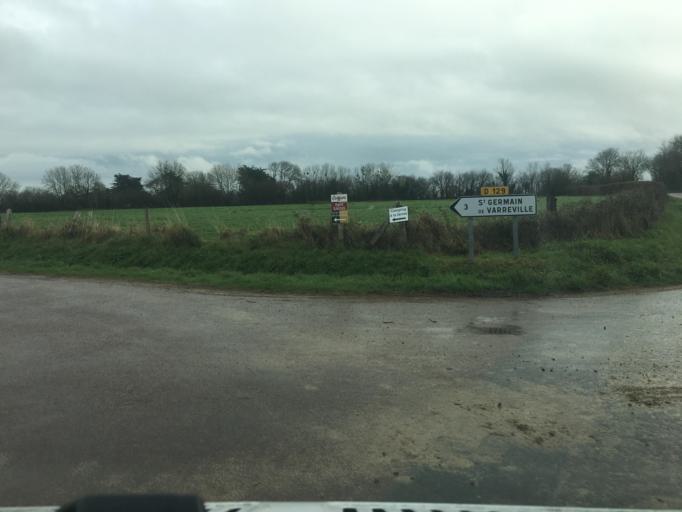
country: FR
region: Lower Normandy
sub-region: Departement de la Manche
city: Sainte-Mere-Eglise
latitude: 49.4203
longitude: -1.2766
